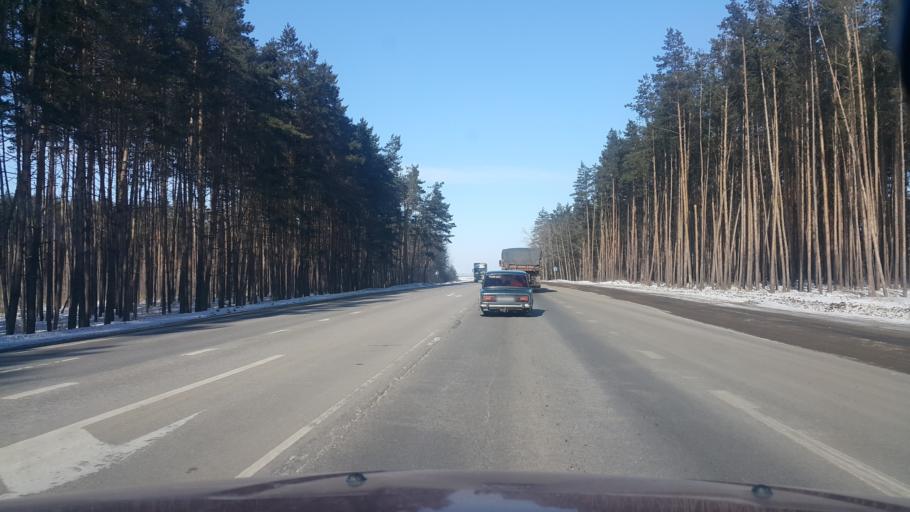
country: RU
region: Tambov
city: Pokrovo-Prigorodnoye
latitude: 52.5918
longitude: 41.3480
